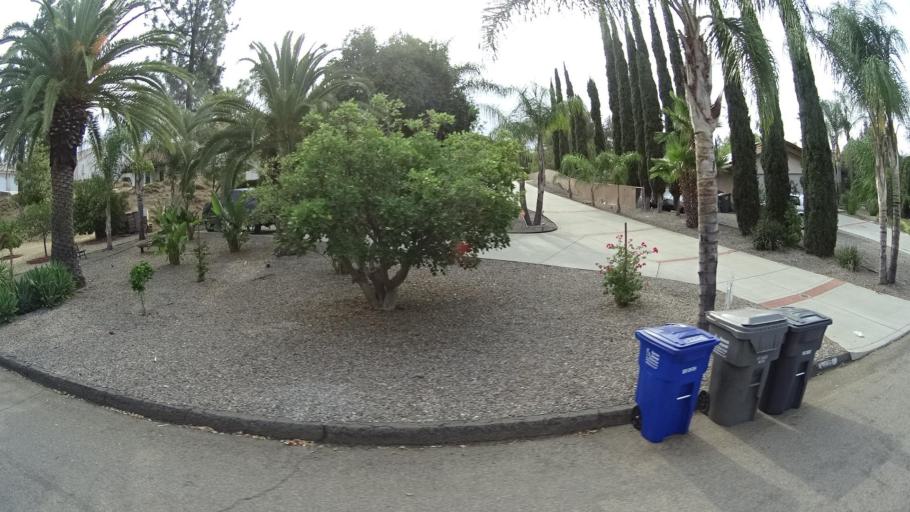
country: US
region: California
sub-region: San Diego County
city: San Diego Country Estates
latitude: 33.0174
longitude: -116.8001
